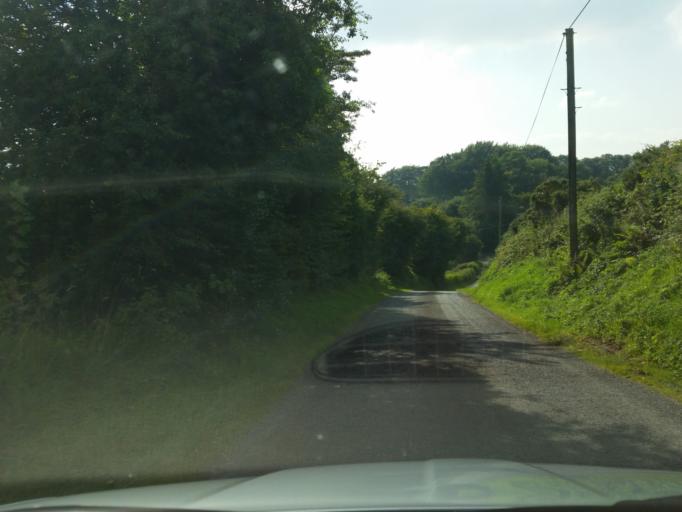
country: GB
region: Northern Ireland
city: Ballinamallard
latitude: 54.3530
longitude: -7.5484
